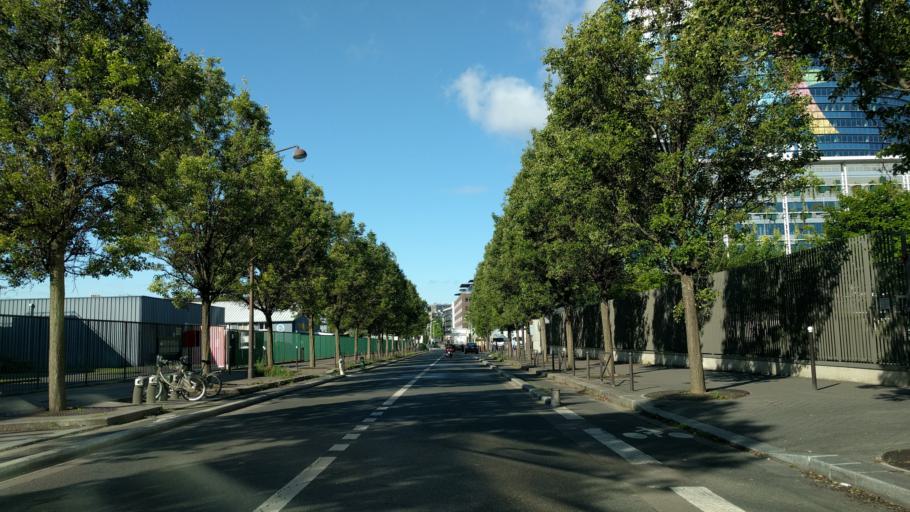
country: FR
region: Ile-de-France
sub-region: Departement des Hauts-de-Seine
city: Issy-les-Moulineaux
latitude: 48.8339
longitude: 2.2714
